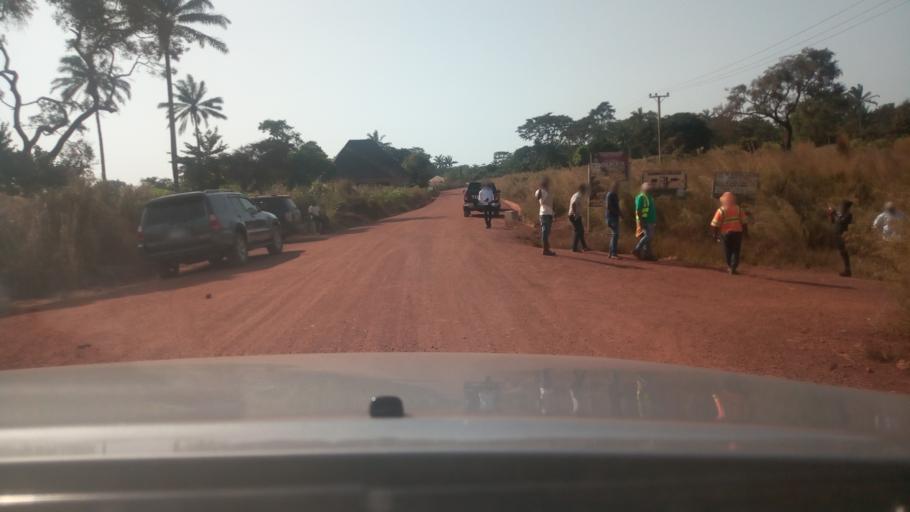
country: NG
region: Enugu
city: Nsukka
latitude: 6.8542
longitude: 7.3546
